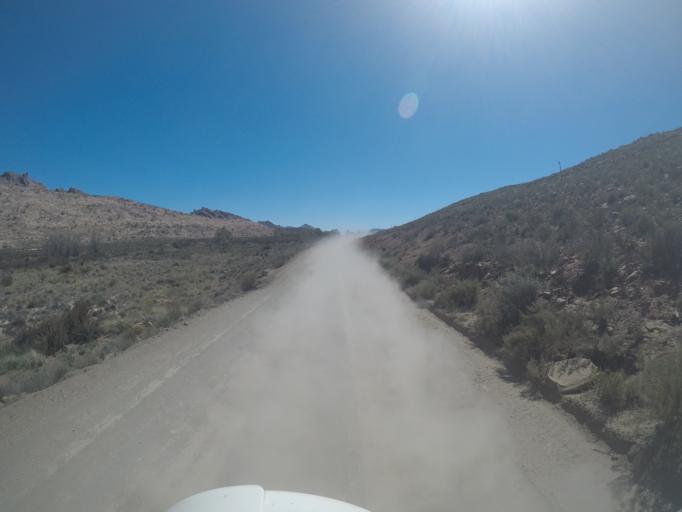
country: ZA
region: Western Cape
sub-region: Cape Winelands District Municipality
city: Ceres
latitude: -32.8200
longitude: 19.4526
